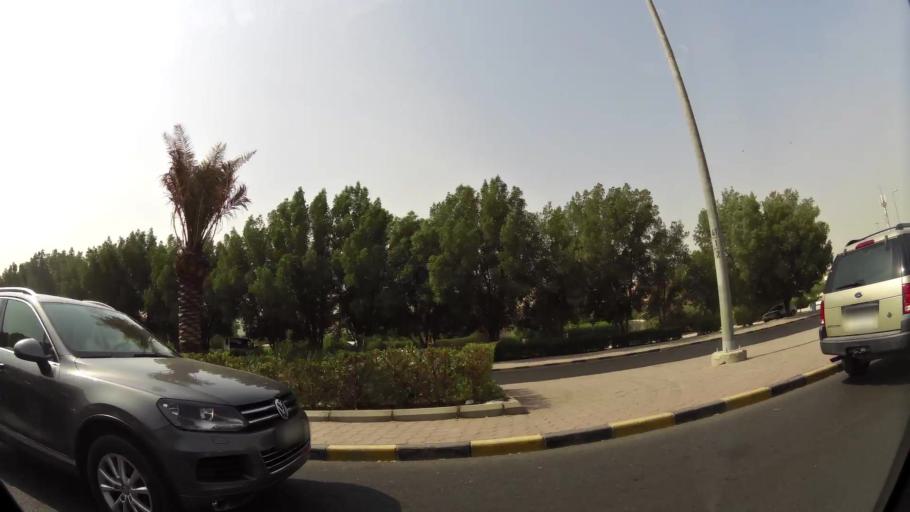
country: KW
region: Al Asimah
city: Ar Rabiyah
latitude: 29.2838
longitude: 47.9066
